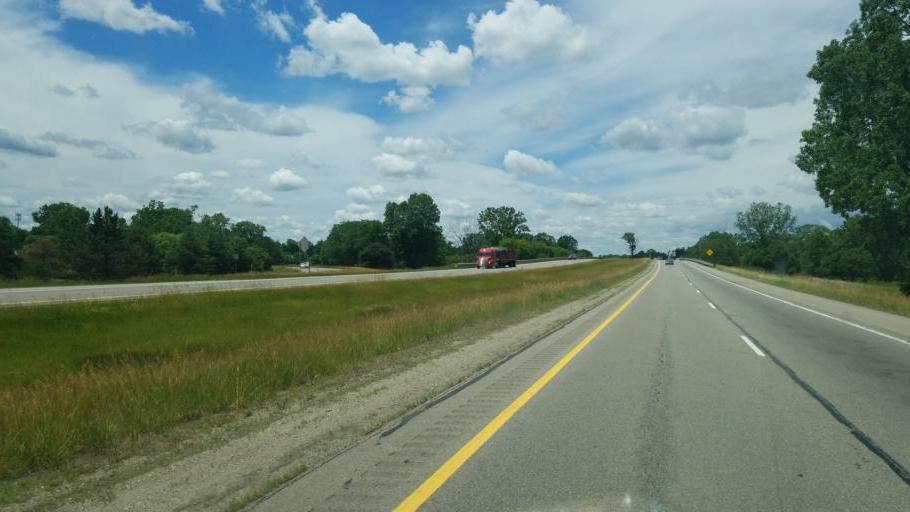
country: US
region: Michigan
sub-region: Eaton County
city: Dimondale
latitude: 42.6642
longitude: -84.5843
